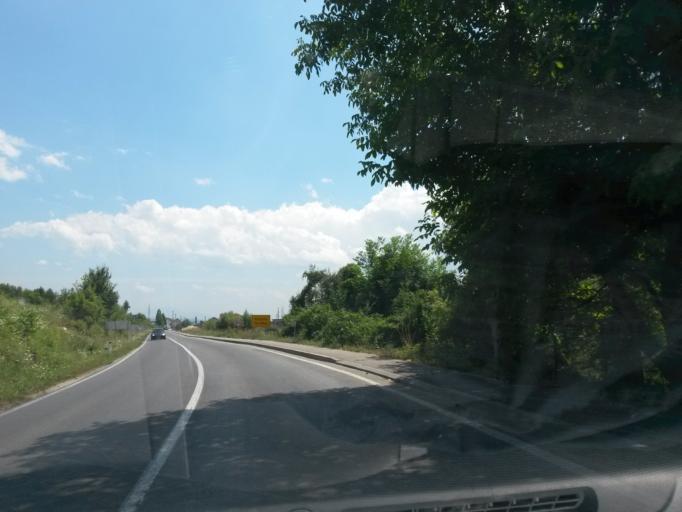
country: BA
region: Federation of Bosnia and Herzegovina
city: Travnik
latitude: 44.2160
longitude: 17.6962
